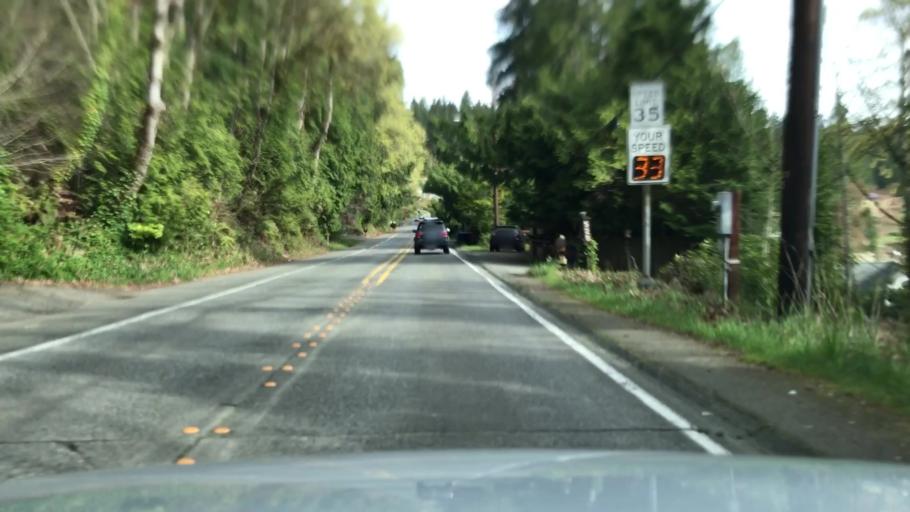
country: US
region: Washington
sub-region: King County
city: West Lake Sammamish
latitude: 47.6036
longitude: -122.1121
